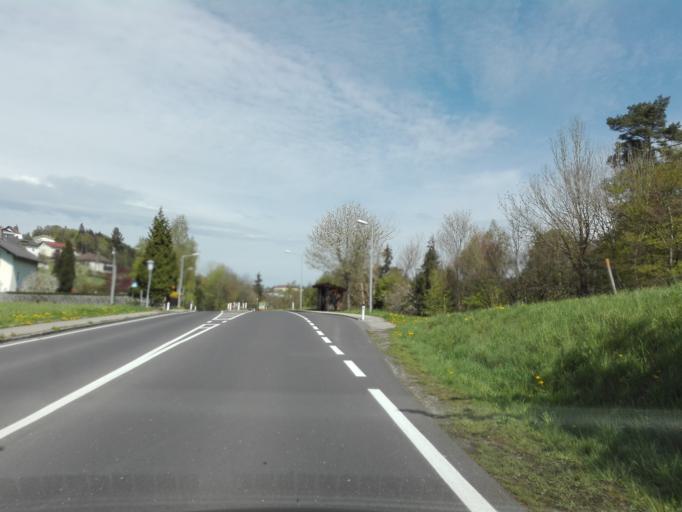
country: AT
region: Upper Austria
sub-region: Linz Stadt
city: Linz
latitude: 48.3367
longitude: 14.2538
